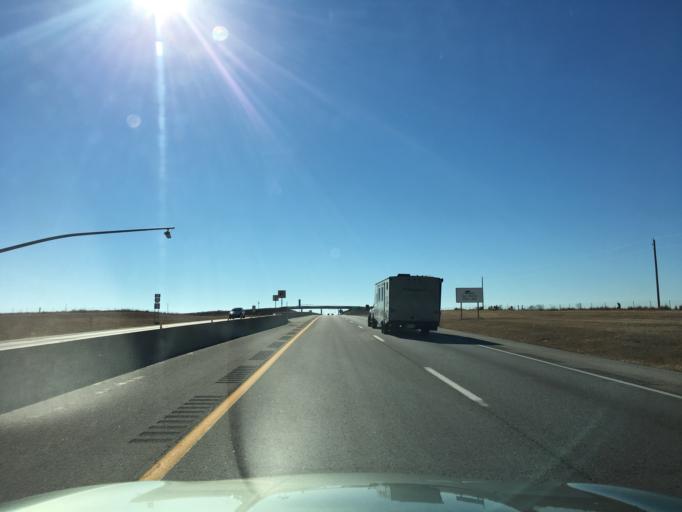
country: US
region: Oklahoma
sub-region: Kay County
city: Blackwell
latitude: 37.0029
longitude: -97.3415
